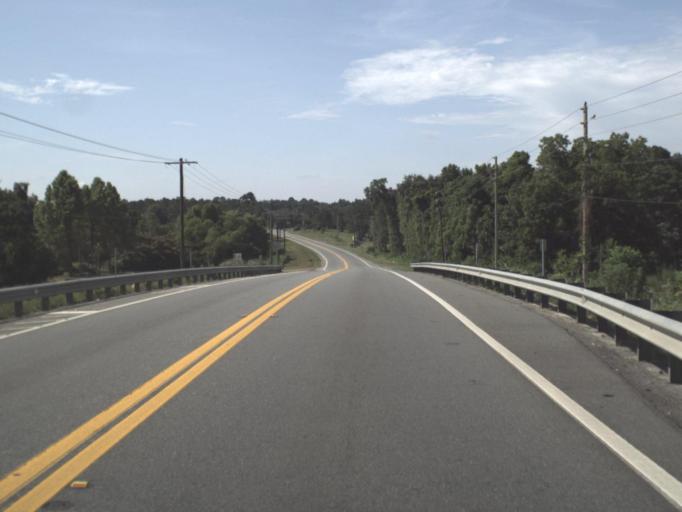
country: US
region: Florida
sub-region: Madison County
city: Madison
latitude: 30.4577
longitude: -83.4093
